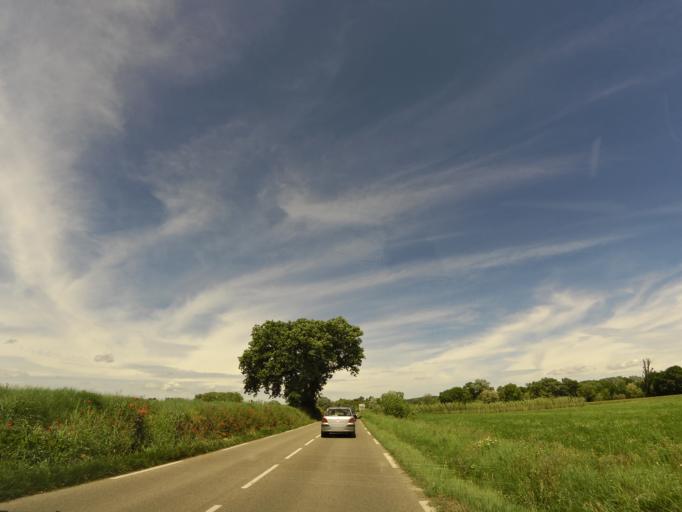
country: FR
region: Languedoc-Roussillon
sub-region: Departement du Gard
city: Sommieres
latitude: 43.7997
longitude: 4.0733
